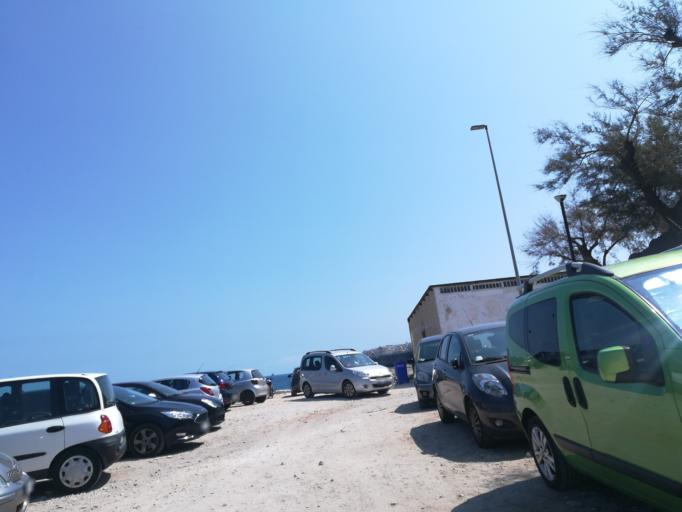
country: IT
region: Apulia
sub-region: Provincia di Bari
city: Polignano a Mare
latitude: 40.9987
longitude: 17.2153
